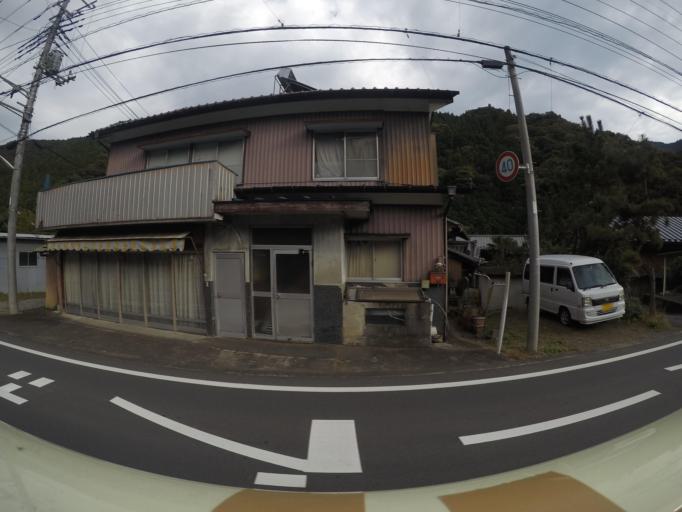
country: JP
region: Gunma
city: Yoshii
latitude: 36.1195
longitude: 138.9410
